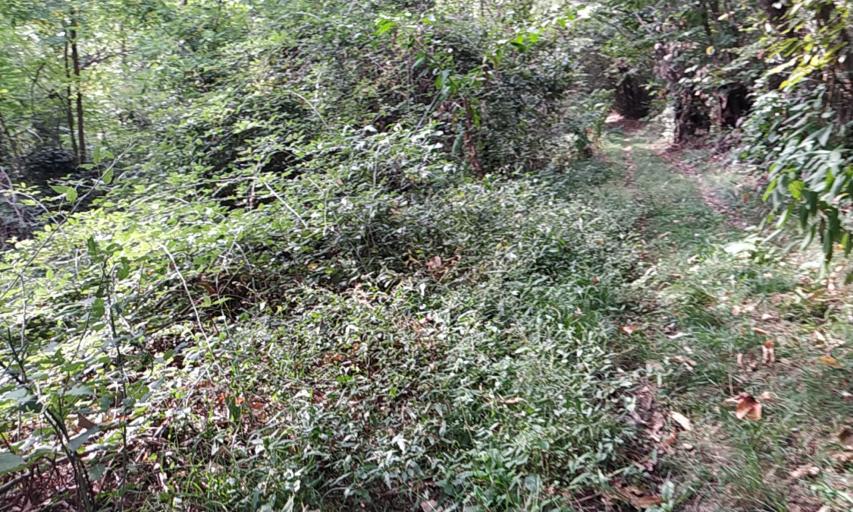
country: IT
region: Piedmont
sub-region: Provincia di Biella
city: Dorzano
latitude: 45.4286
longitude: 8.0942
